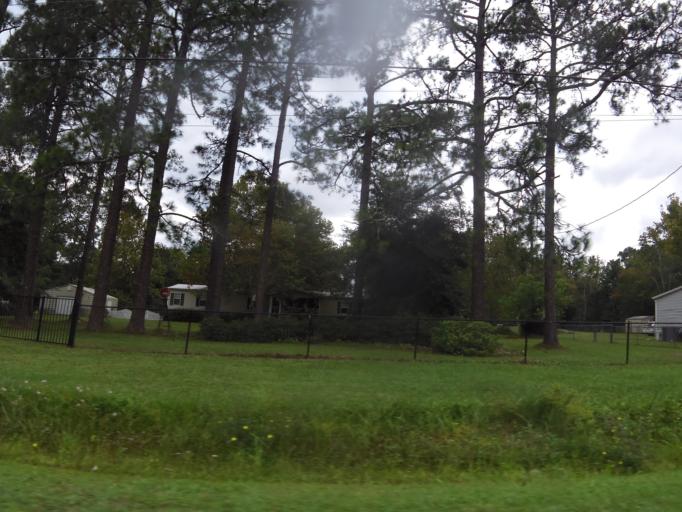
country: US
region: Florida
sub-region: Clay County
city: Middleburg
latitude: 30.0963
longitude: -81.9491
